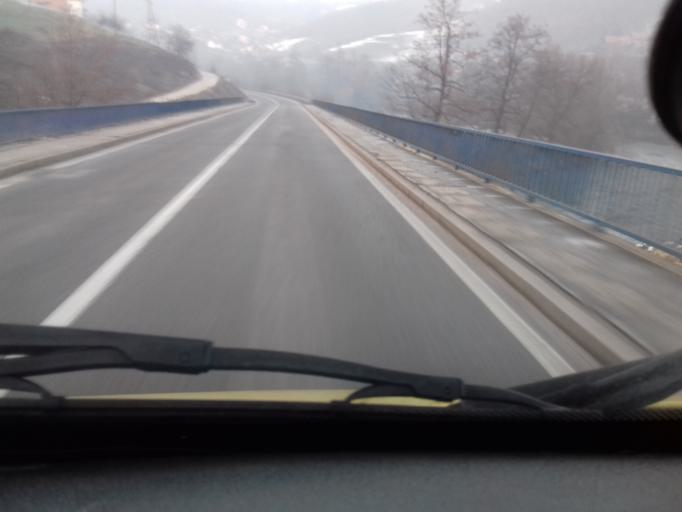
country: BA
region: Federation of Bosnia and Herzegovina
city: Vogosca
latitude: 43.8866
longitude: 18.3255
